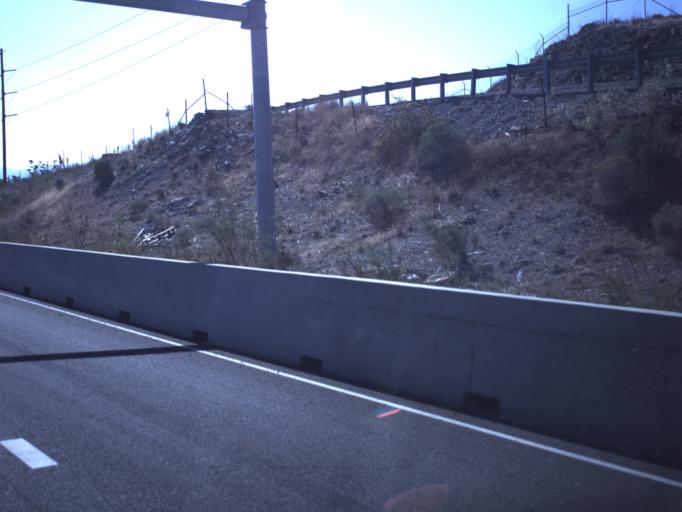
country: US
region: Utah
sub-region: Salt Lake County
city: Magna
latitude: 40.7280
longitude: -112.1731
